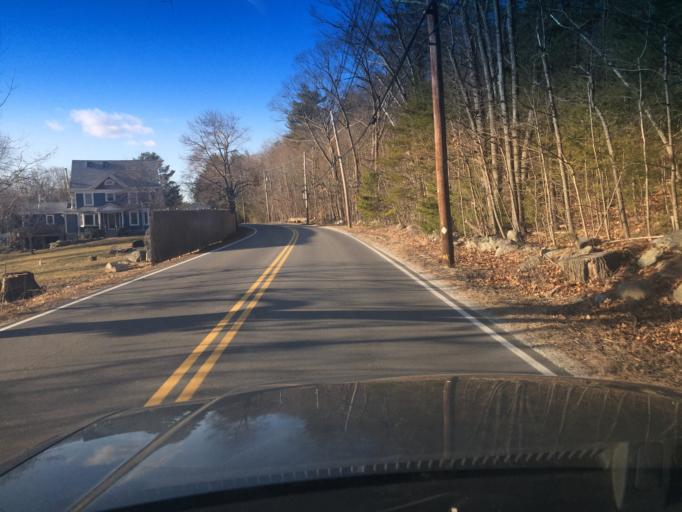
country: US
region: Massachusetts
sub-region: Middlesex County
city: Sherborn
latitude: 42.2576
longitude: -71.3714
